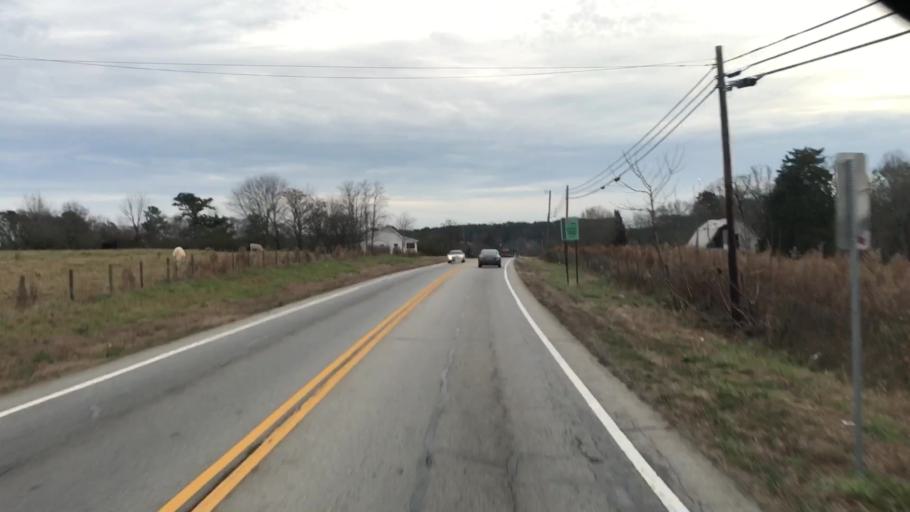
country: US
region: Georgia
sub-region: Barrow County
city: Winder
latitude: 34.0150
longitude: -83.7587
